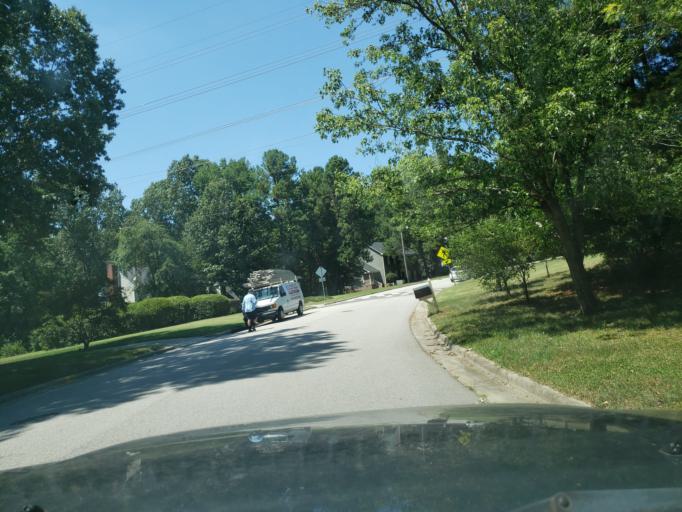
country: US
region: North Carolina
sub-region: Durham County
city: Durham
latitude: 35.9187
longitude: -78.9435
